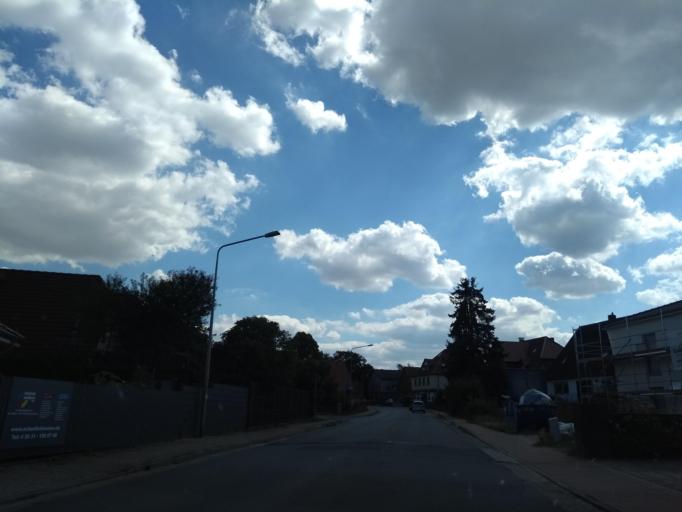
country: DE
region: Lower Saxony
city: Wunstorf
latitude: 52.4507
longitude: 9.4194
